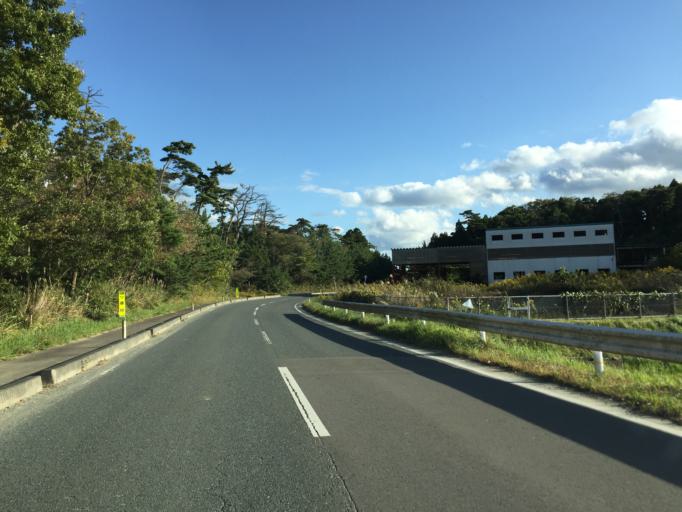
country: JP
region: Miyagi
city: Marumori
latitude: 37.8565
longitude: 140.9444
